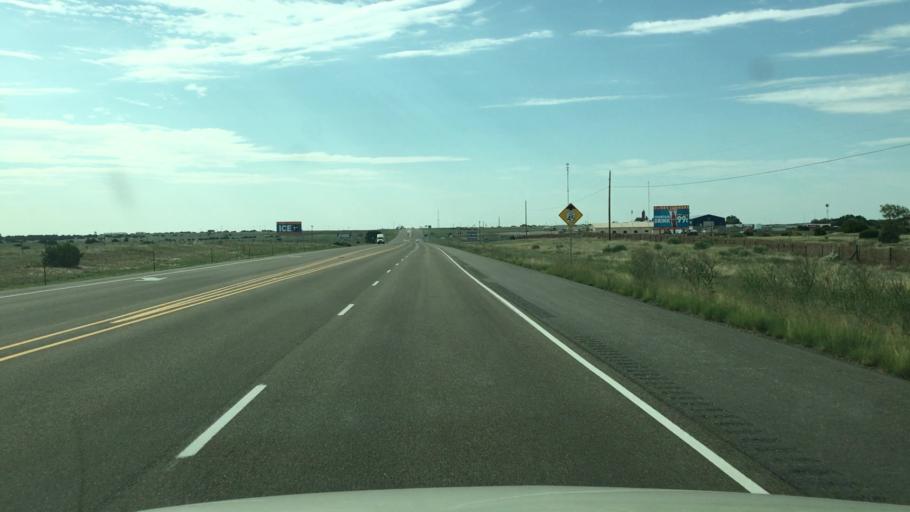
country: US
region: New Mexico
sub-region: Torrance County
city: Moriarty
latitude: 35.0193
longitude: -105.6705
